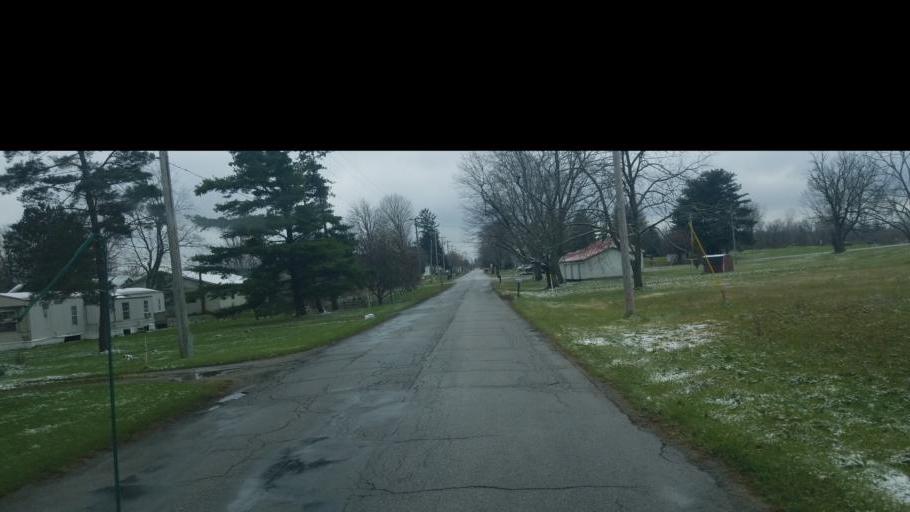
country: US
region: Ohio
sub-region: Richland County
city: Shelby
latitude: 40.8980
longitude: -82.6553
